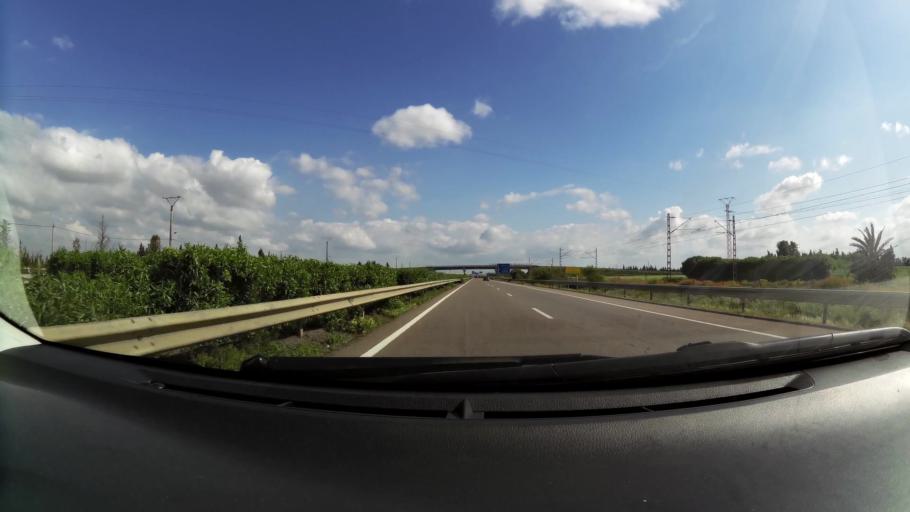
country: MA
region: Chaouia-Ouardigha
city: Nouaseur
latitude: 33.3356
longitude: -7.6102
